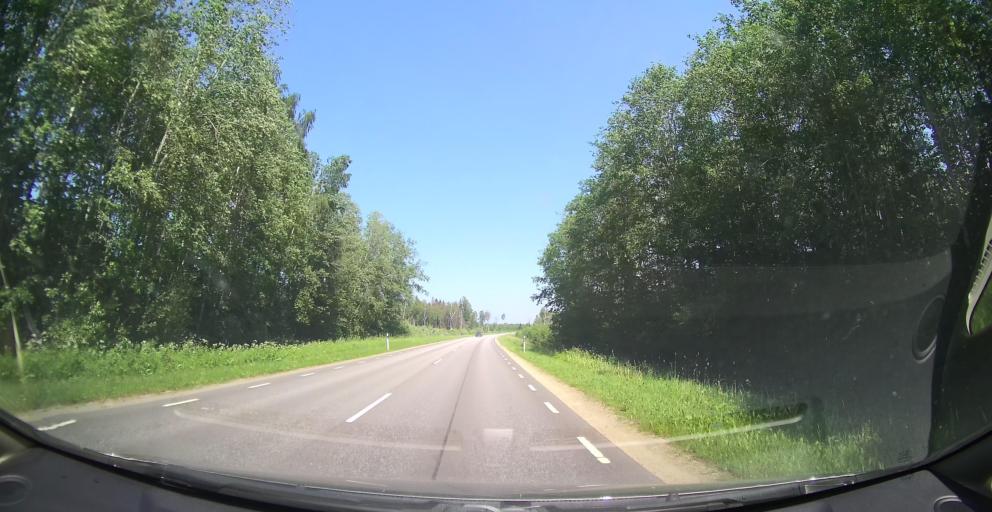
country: EE
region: Harju
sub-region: Anija vald
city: Kehra
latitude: 59.2416
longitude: 25.2955
